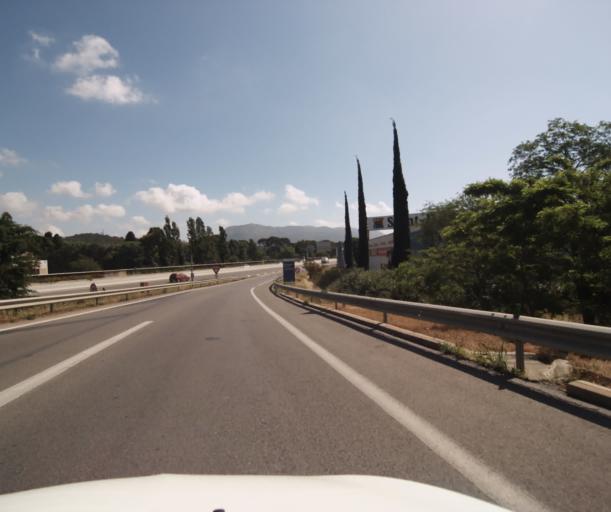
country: FR
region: Provence-Alpes-Cote d'Azur
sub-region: Departement du Var
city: La Seyne-sur-Mer
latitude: 43.1253
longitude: 5.8790
